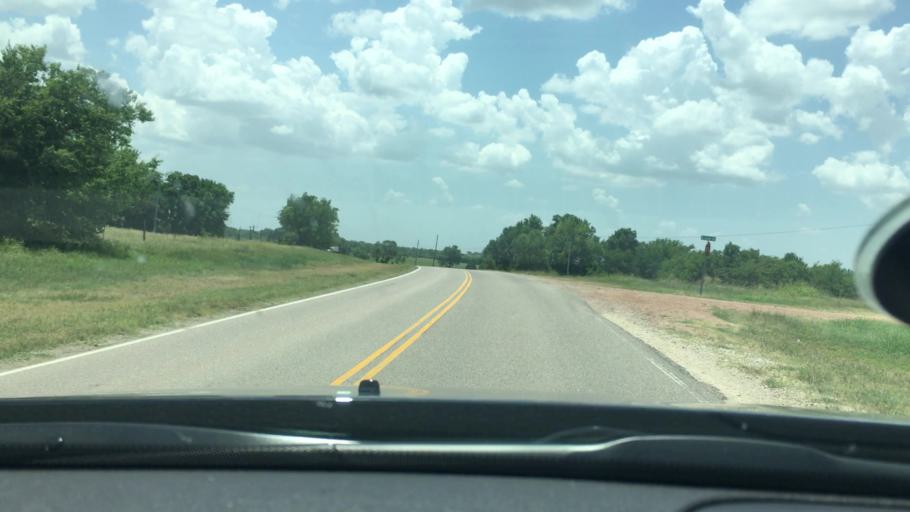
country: US
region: Oklahoma
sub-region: Johnston County
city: Tishomingo
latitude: 34.4723
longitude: -96.6355
